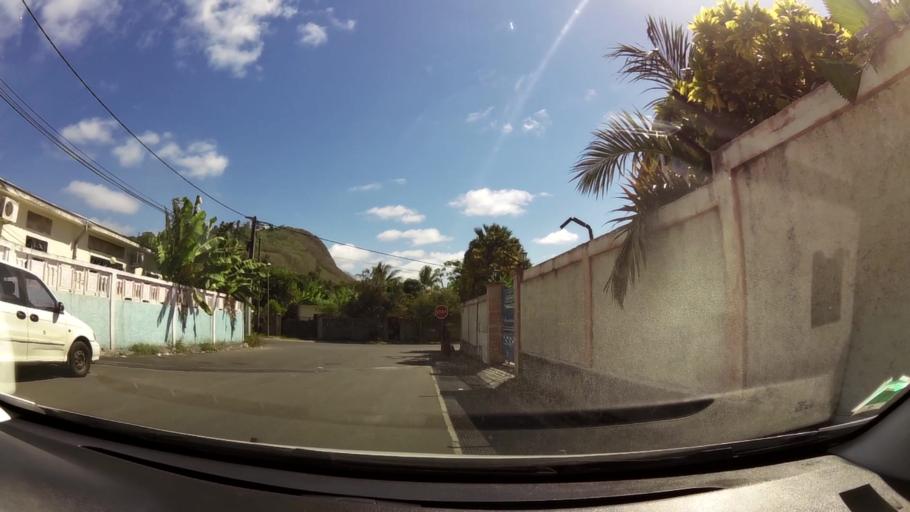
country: YT
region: Pamandzi
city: Pamandzi
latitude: -12.7909
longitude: 45.2803
